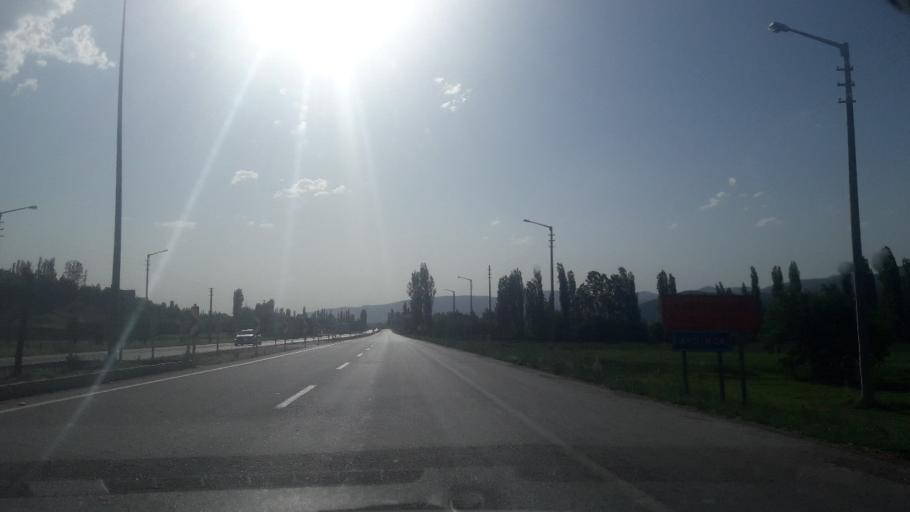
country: TR
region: Amasya
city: Ezinepazari
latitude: 40.5712
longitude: 36.1314
